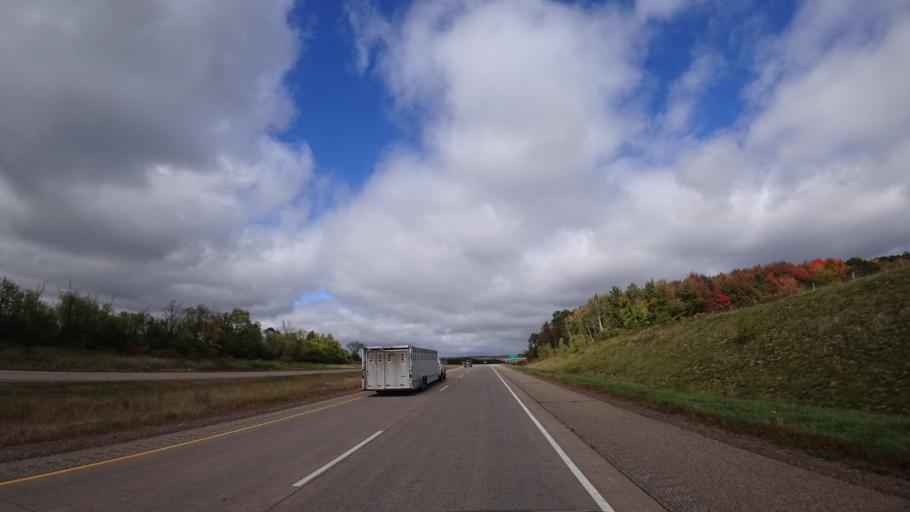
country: US
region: Wisconsin
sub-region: Chippewa County
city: Chippewa Falls
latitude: 44.9070
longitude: -91.3725
